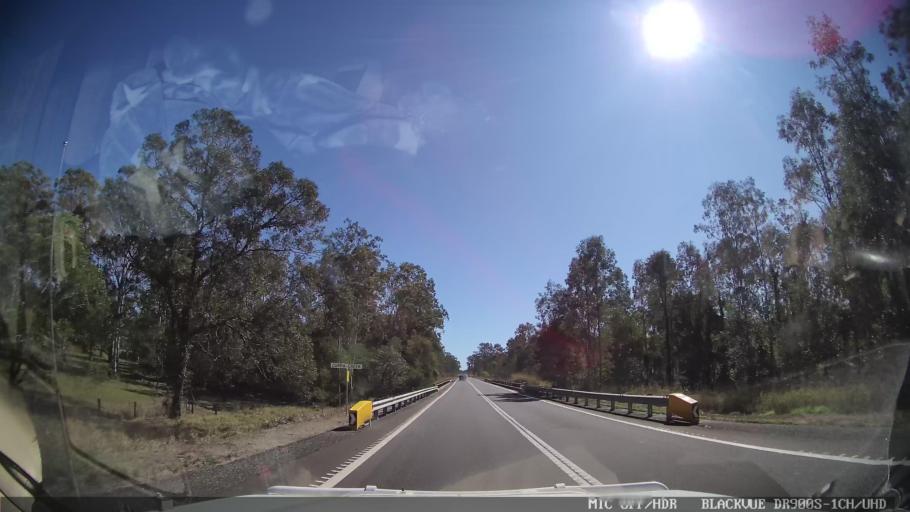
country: AU
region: Queensland
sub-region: Gympie Regional Council
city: Gympie
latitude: -26.0430
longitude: 152.5718
